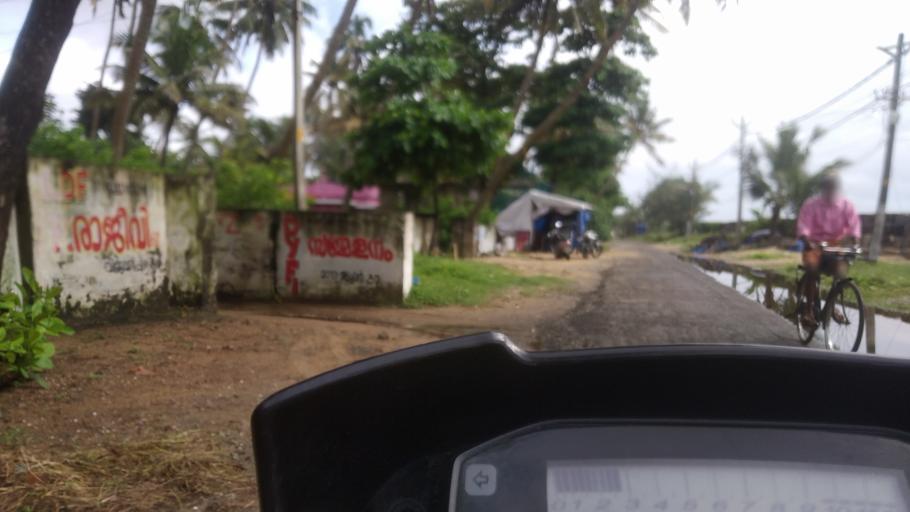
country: IN
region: Kerala
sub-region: Thrissur District
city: Kodungallur
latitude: 10.1343
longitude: 76.1809
